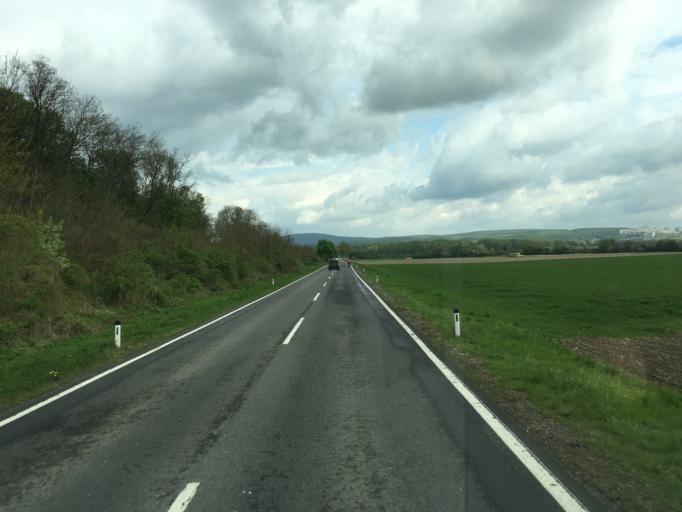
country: AT
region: Lower Austria
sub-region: Politischer Bezirk Bruck an der Leitha
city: Berg
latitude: 48.1201
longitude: 17.0332
